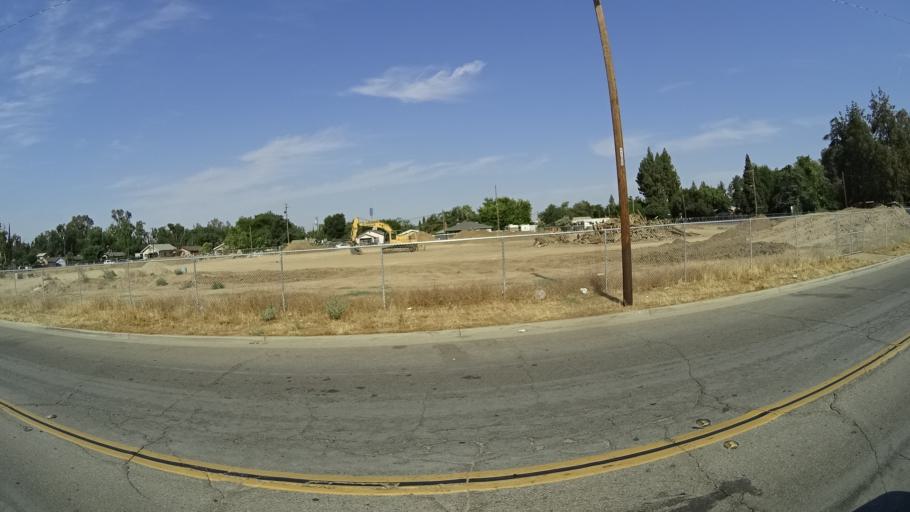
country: US
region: California
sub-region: Fresno County
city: Fresno
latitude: 36.7496
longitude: -119.8209
